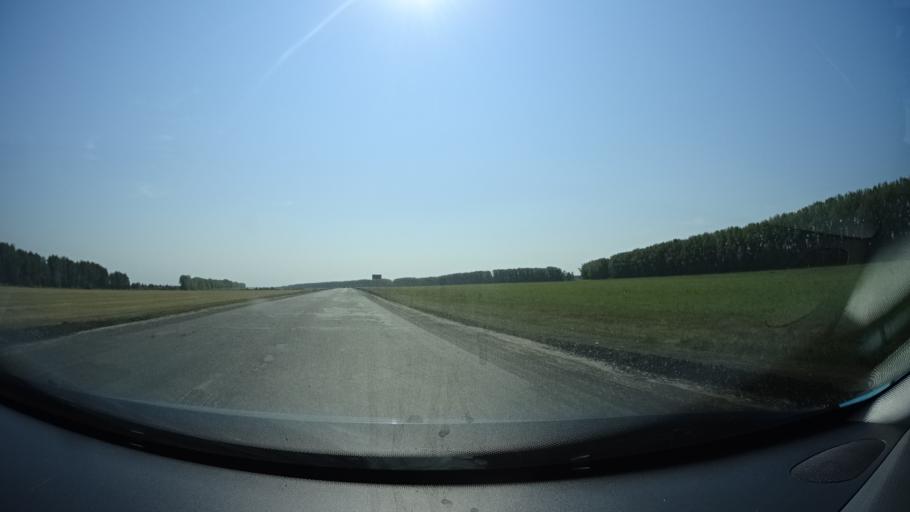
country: RU
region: Bashkortostan
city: Kabakovo
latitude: 54.4627
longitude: 55.9626
